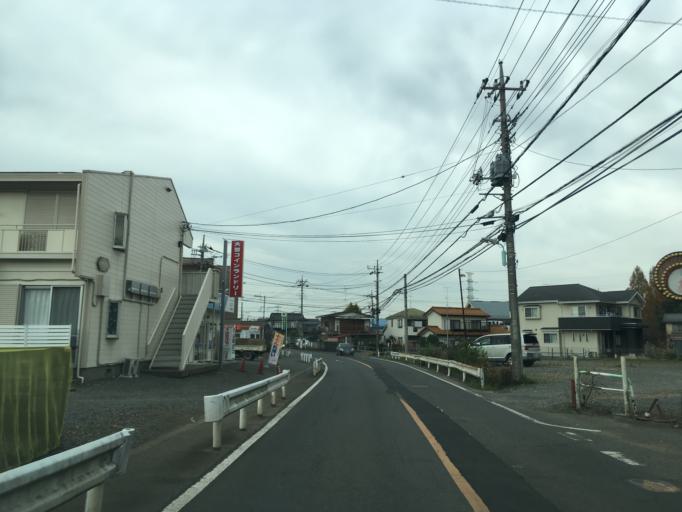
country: JP
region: Saitama
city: Tokorozawa
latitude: 35.7786
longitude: 139.4520
